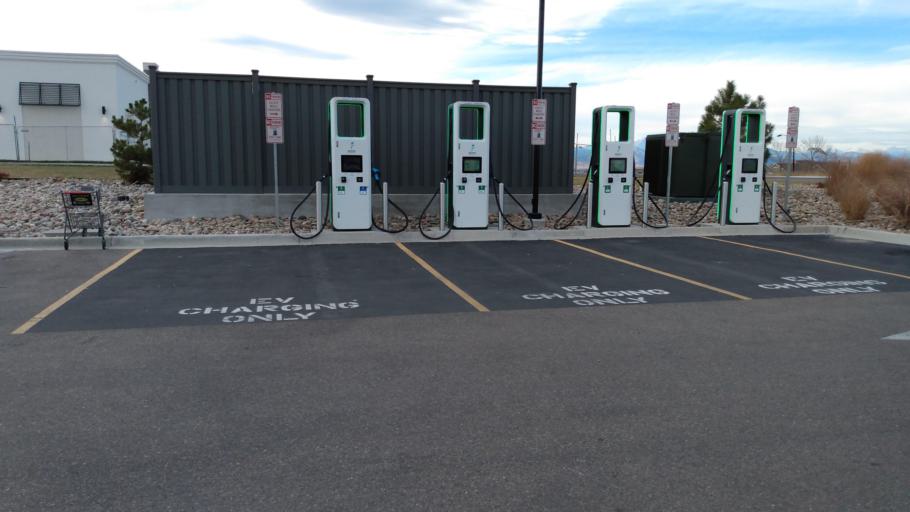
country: US
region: Colorado
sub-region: Boulder County
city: Erie
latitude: 40.0024
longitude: -105.0113
